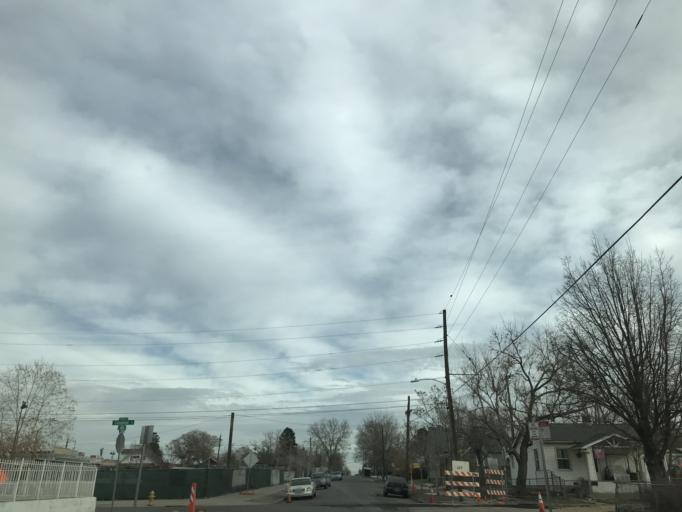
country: US
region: Colorado
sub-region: Adams County
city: Commerce City
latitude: 39.7790
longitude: -104.9575
